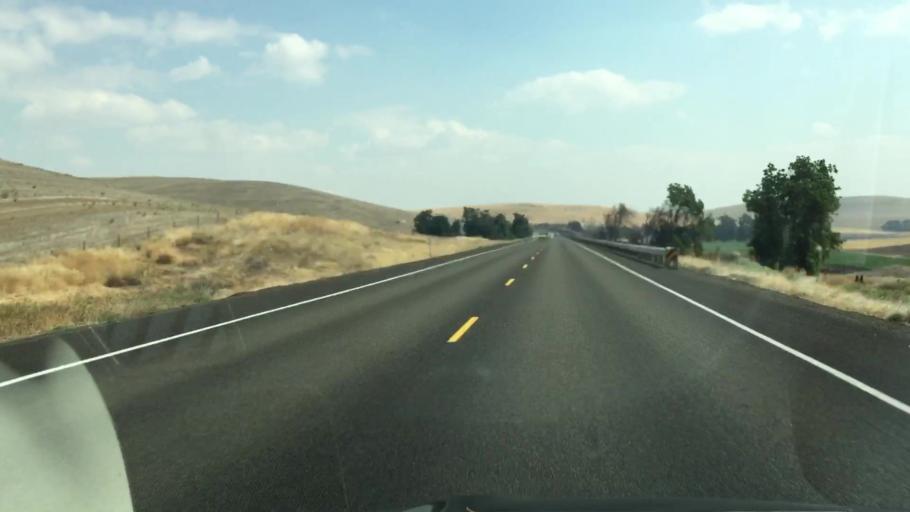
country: US
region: Oregon
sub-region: Wasco County
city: The Dalles
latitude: 45.4884
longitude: -121.1061
